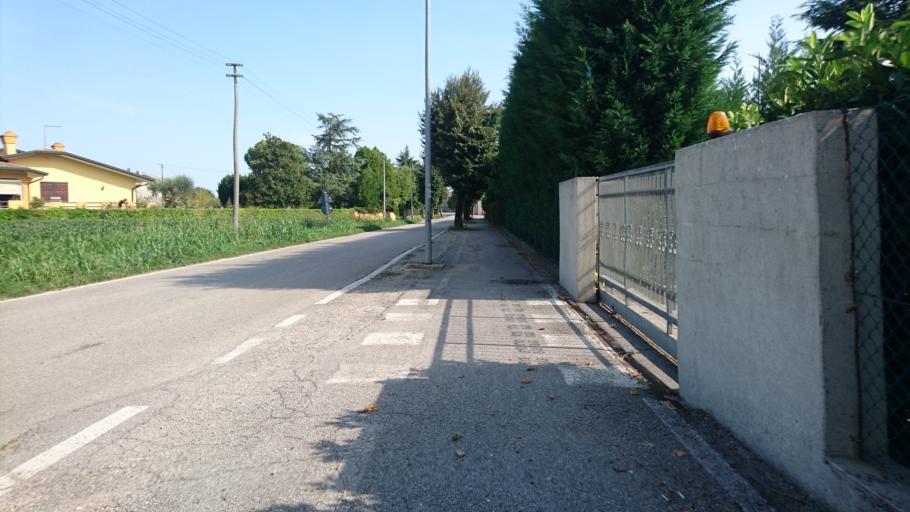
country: IT
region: Veneto
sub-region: Provincia di Padova
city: Saccolongo
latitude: 45.4132
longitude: 11.7477
